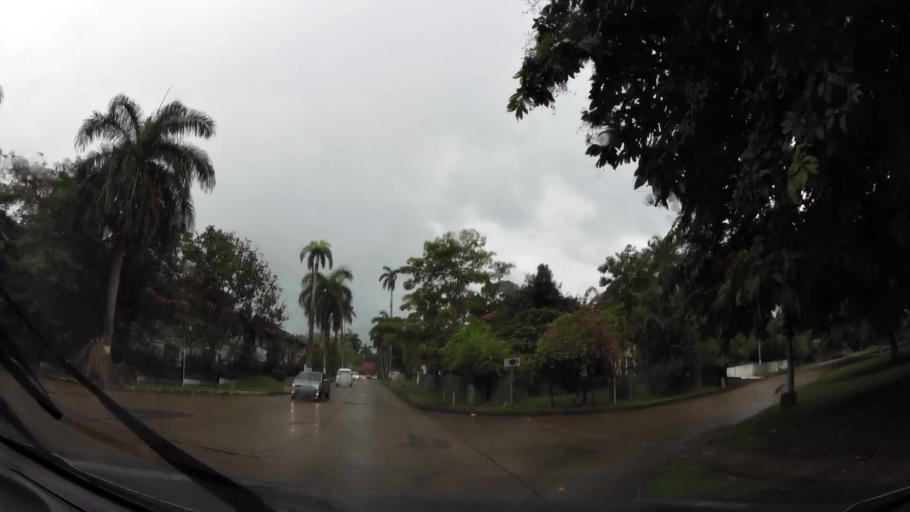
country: PA
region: Panama
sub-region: Distrito de Panama
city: Ancon
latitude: 8.9764
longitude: -79.5583
